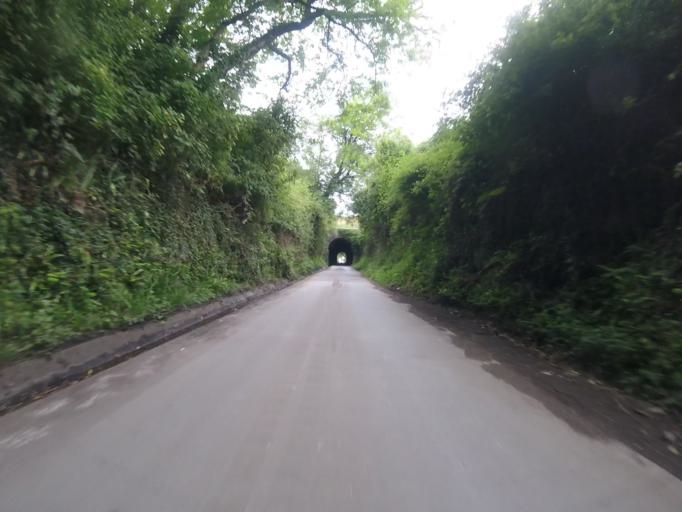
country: ES
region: Navarre
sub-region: Provincia de Navarra
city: Sunbilla
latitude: 43.1635
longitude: -1.6710
